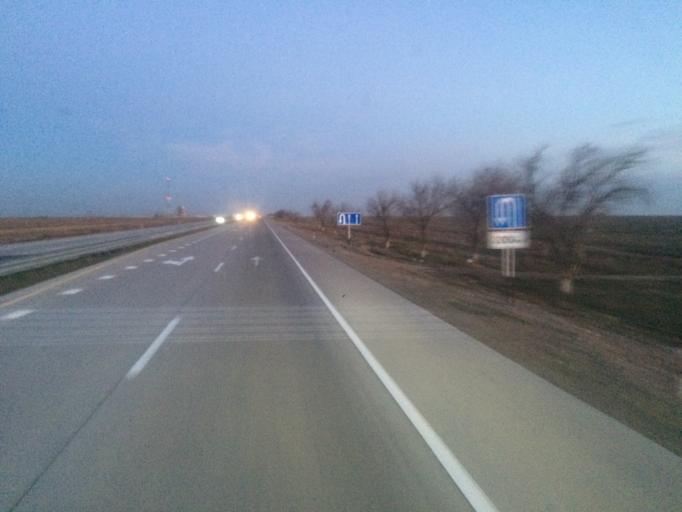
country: KZ
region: Ongtustik Qazaqstan
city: Temirlanovka
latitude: 42.8350
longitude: 69.1179
